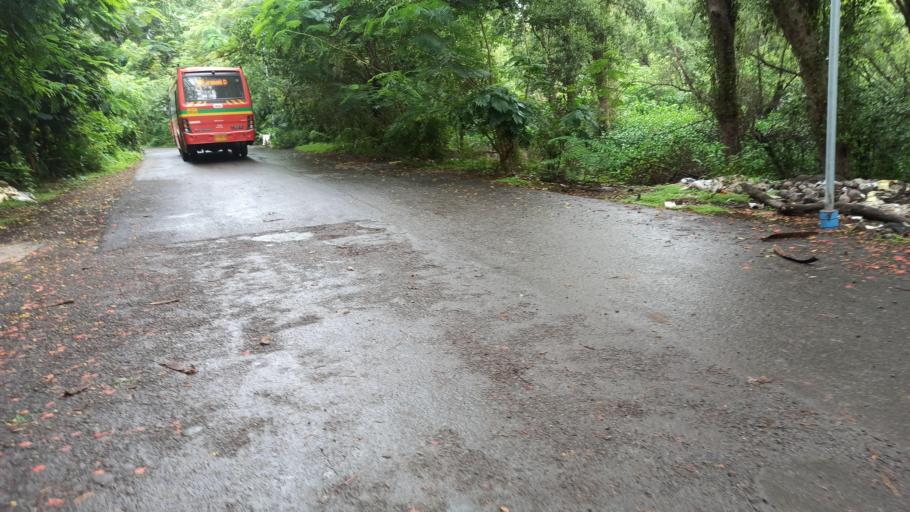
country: IN
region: Maharashtra
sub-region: Mumbai Suburban
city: Borivli
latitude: 19.2637
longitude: 72.8607
